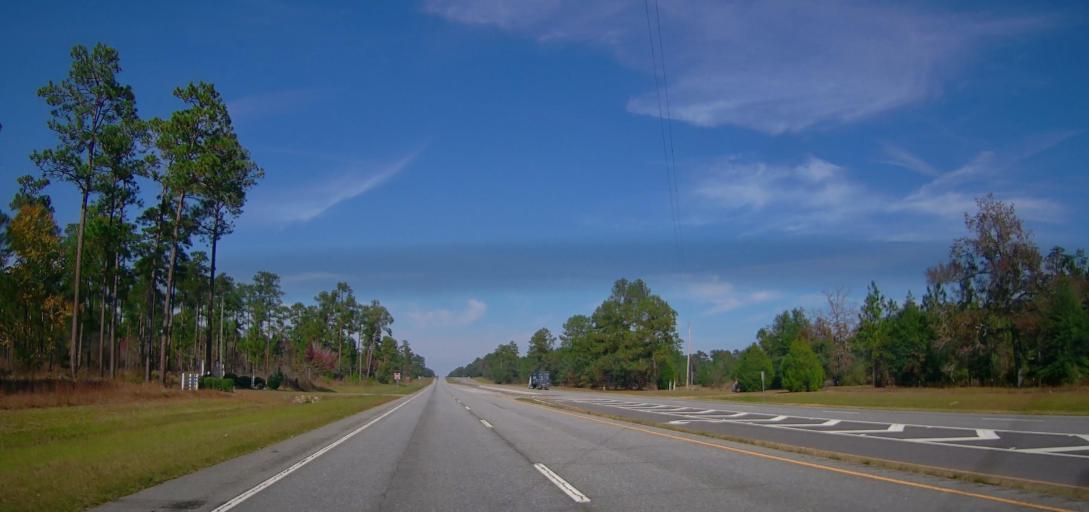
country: US
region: Georgia
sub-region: Dougherty County
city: Albany
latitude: 31.6691
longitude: -83.9965
